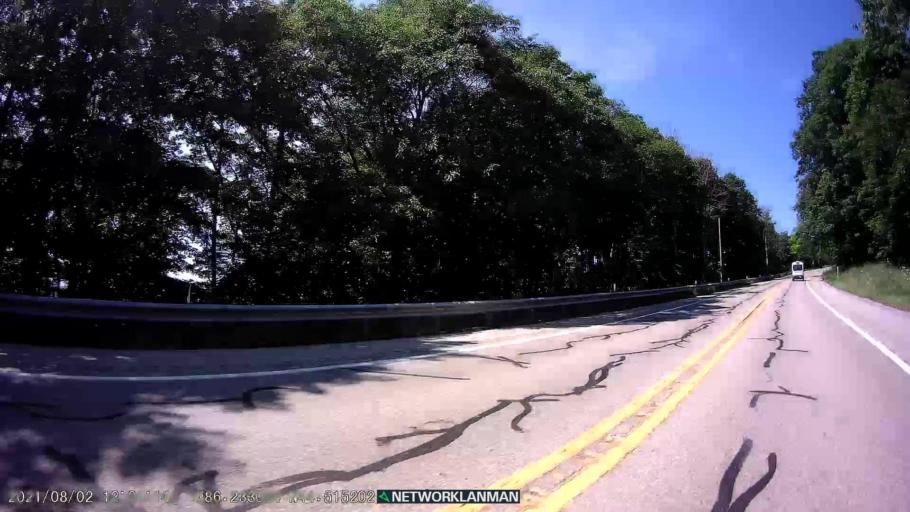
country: US
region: Michigan
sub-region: Benzie County
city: Frankfort
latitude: 44.5154
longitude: -86.2332
